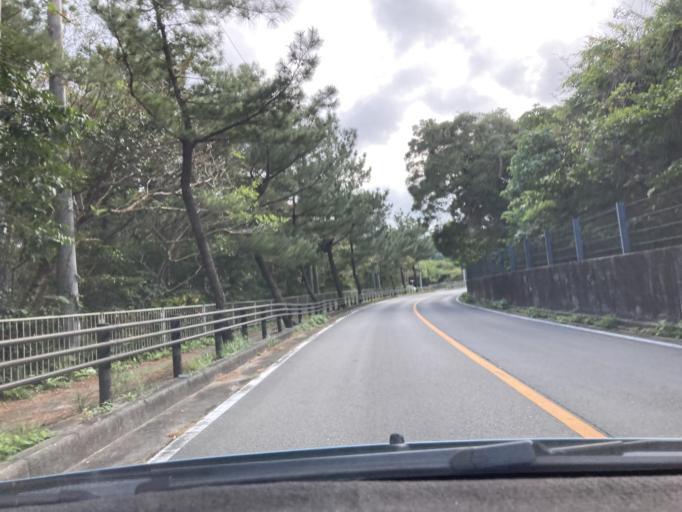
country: JP
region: Okinawa
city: Nago
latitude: 26.8598
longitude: 128.2612
